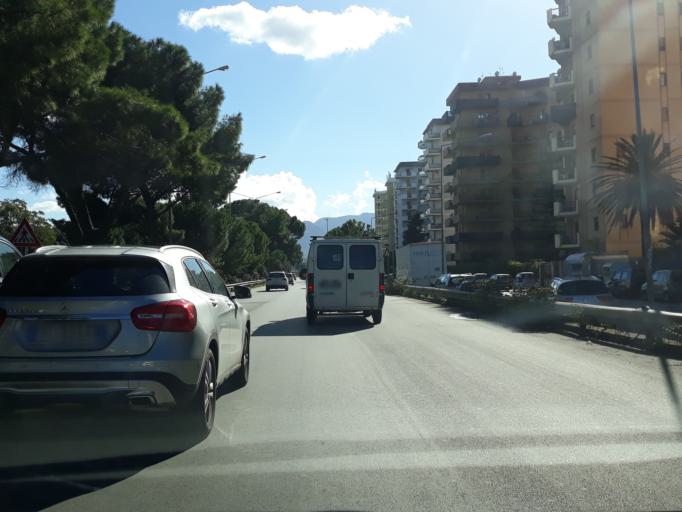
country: IT
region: Sicily
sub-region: Palermo
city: Palermo
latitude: 38.1340
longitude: 13.3303
